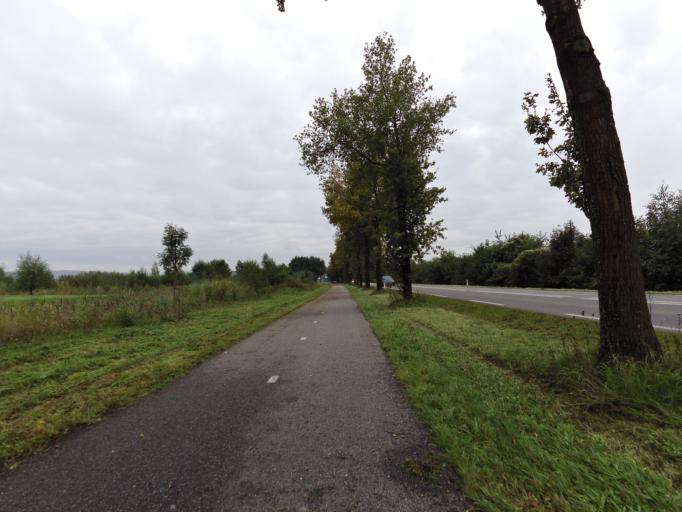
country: NL
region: Gelderland
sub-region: Oude IJsselstreek
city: Gendringen
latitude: 51.9009
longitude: 6.3557
